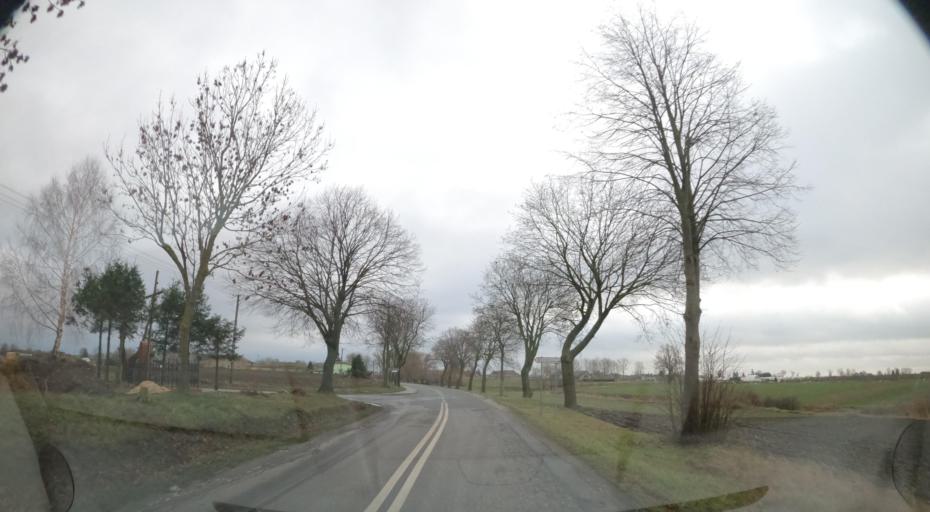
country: PL
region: Greater Poland Voivodeship
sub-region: Powiat pilski
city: Lobzenica
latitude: 53.2596
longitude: 17.2401
